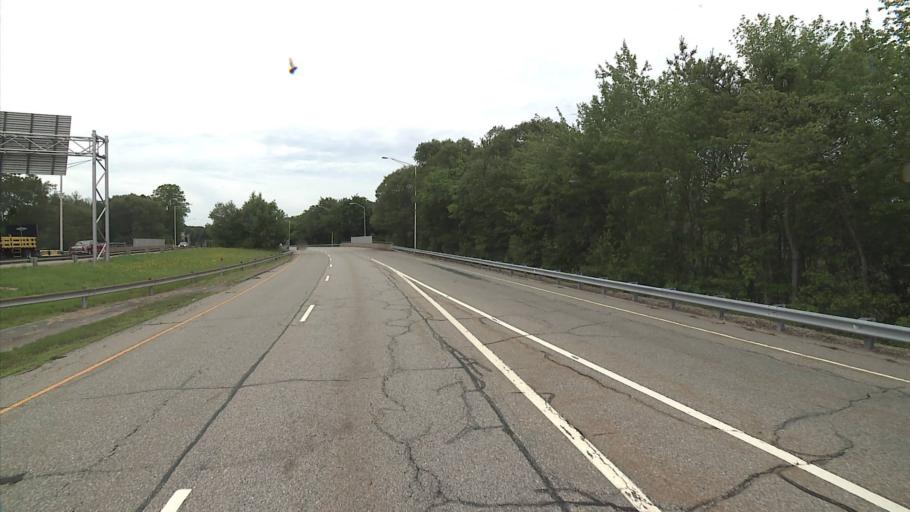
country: US
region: Connecticut
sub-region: New London County
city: Groton
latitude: 41.3590
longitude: -72.0675
